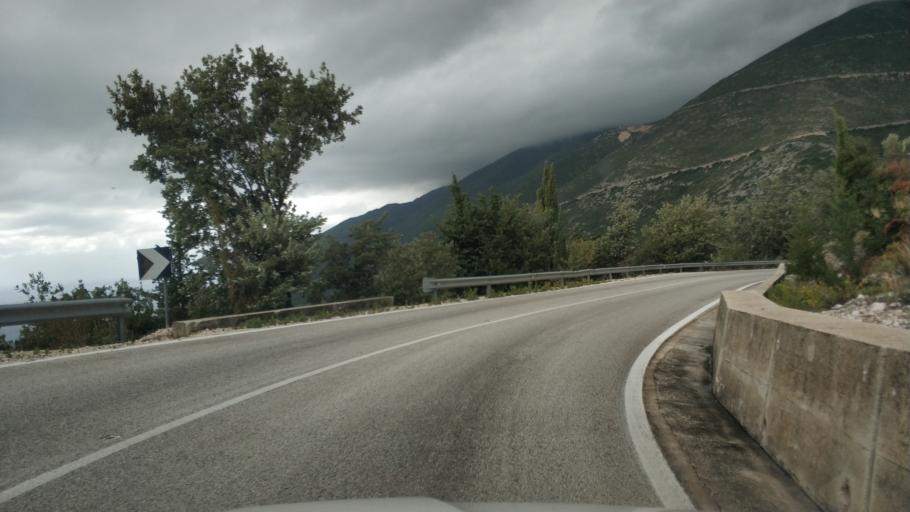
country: AL
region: Vlore
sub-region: Rrethi i Vlores
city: Vranisht
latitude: 40.1712
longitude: 19.6133
